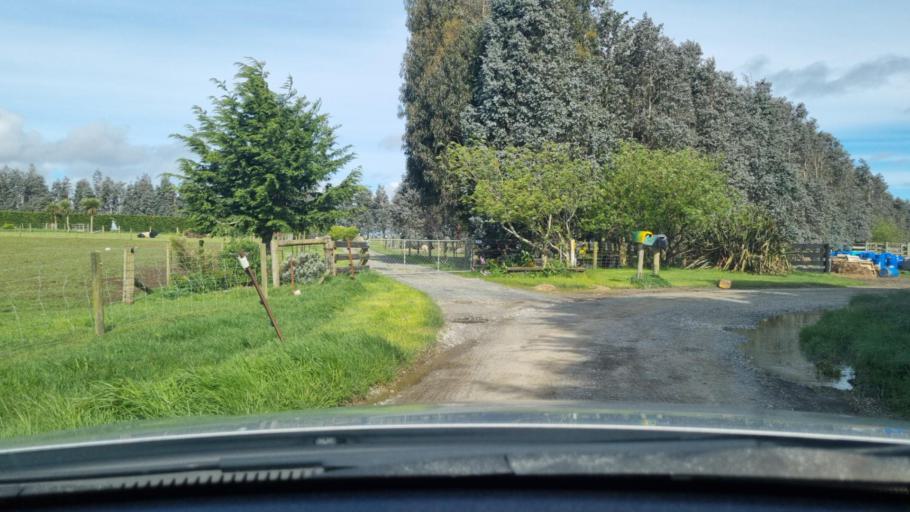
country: NZ
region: Southland
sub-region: Invercargill City
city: Invercargill
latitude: -46.4543
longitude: 168.3792
